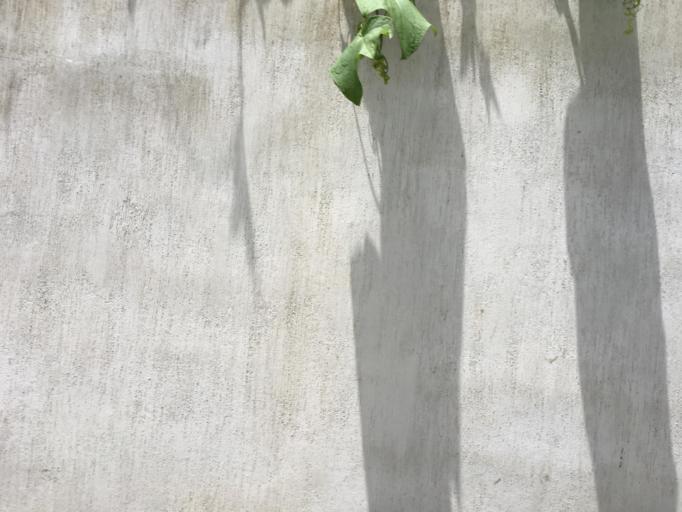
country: GT
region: Sacatepequez
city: Ciudad Vieja
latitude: 14.5237
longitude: -90.7497
